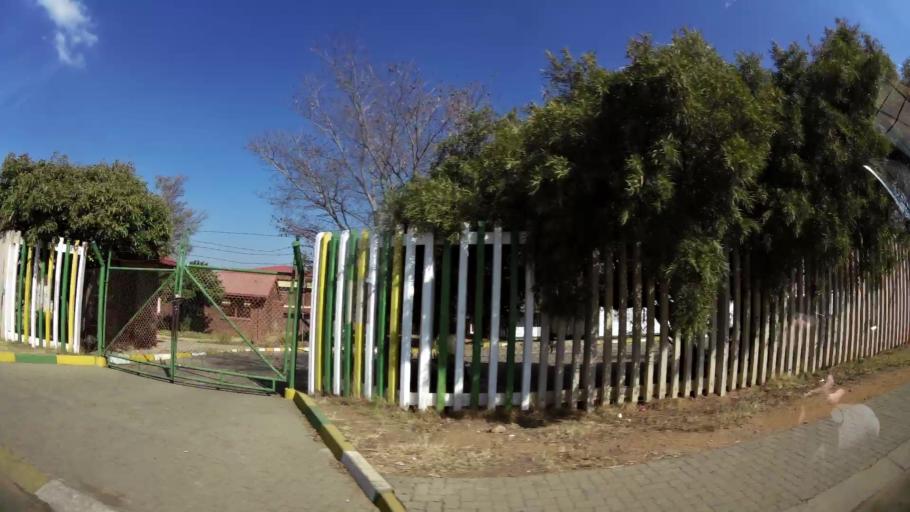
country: ZA
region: Gauteng
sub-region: City of Johannesburg Metropolitan Municipality
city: Roodepoort
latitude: -26.1684
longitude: 27.7988
